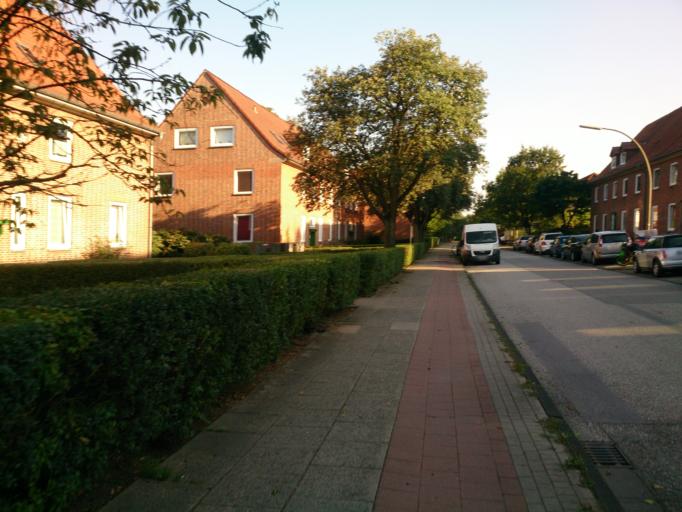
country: DE
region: Hamburg
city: Altona
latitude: 53.5300
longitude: 9.8593
